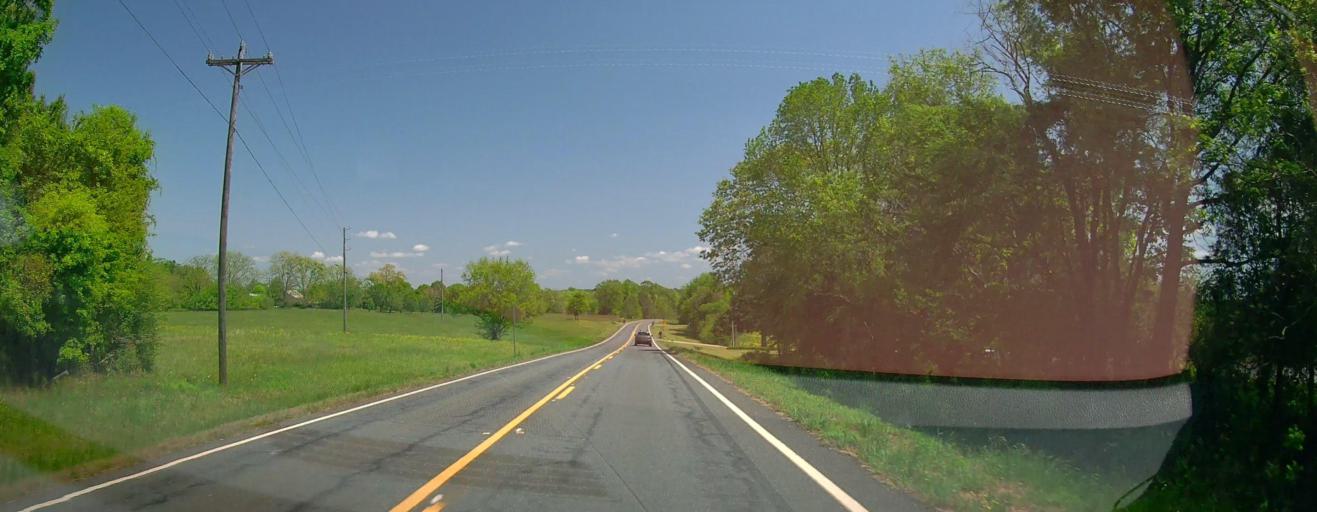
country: US
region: Georgia
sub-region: Jasper County
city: Monticello
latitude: 33.2737
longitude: -83.5943
